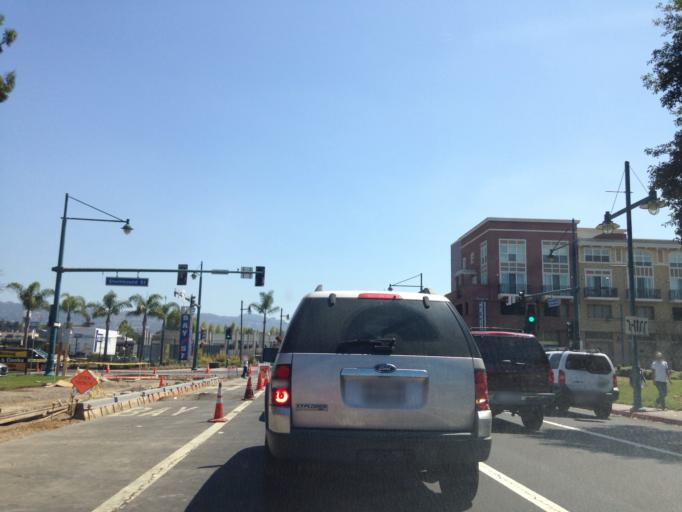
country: US
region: California
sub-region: Alameda County
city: Emeryville
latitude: 37.8371
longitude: -122.2938
